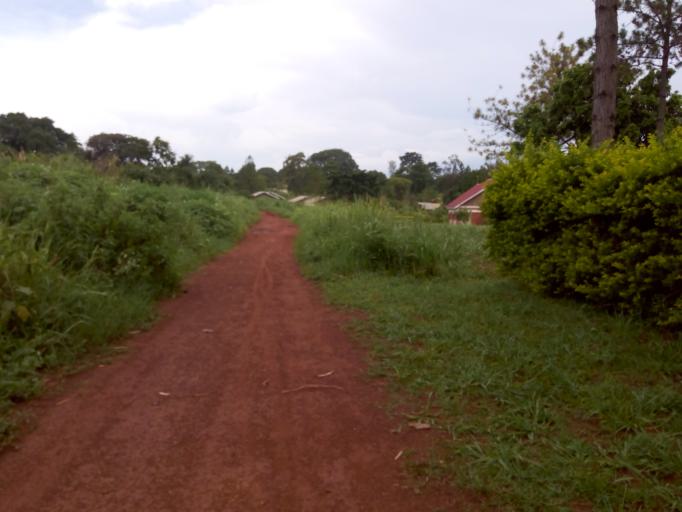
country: UG
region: Western Region
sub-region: Masindi District
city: Masindi
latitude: 1.6880
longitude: 31.7134
